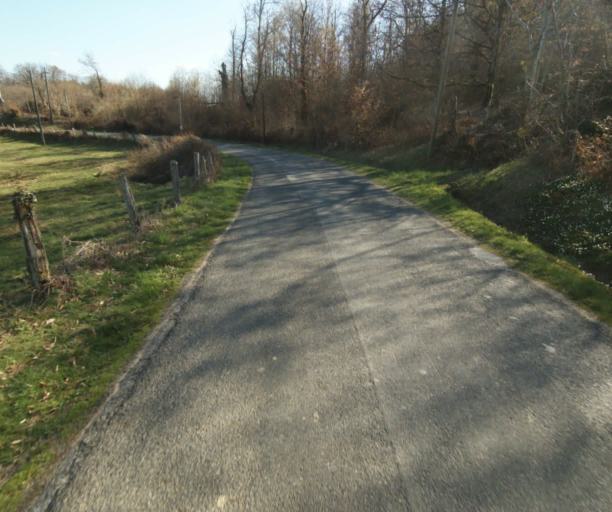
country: FR
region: Limousin
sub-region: Departement de la Correze
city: Saint-Mexant
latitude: 45.3130
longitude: 1.6135
